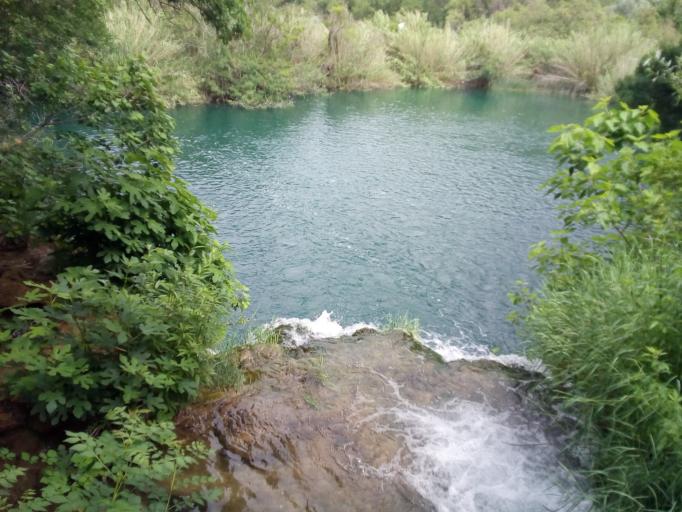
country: HR
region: Sibensko-Kniniska
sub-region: Grad Sibenik
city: Sibenik
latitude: 43.8042
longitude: 15.9665
